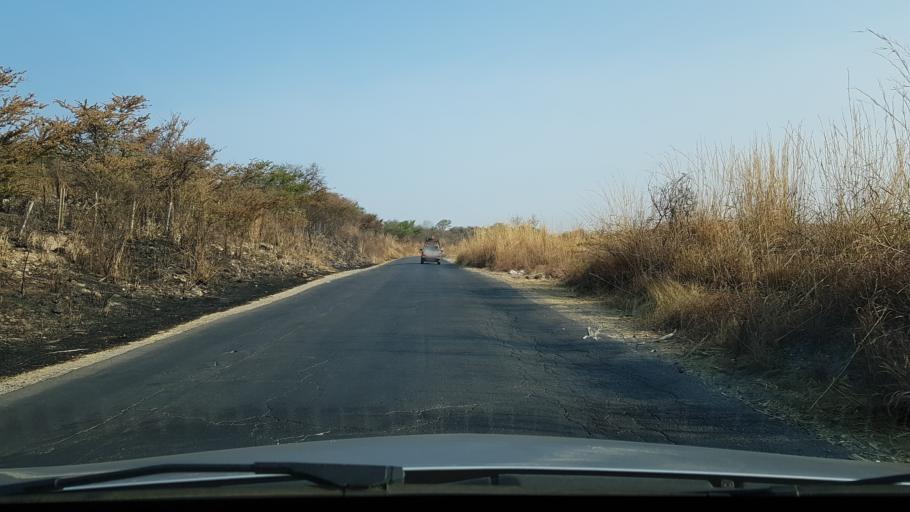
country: MX
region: Morelos
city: Tlaltizapan
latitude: 18.6594
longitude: -99.0458
